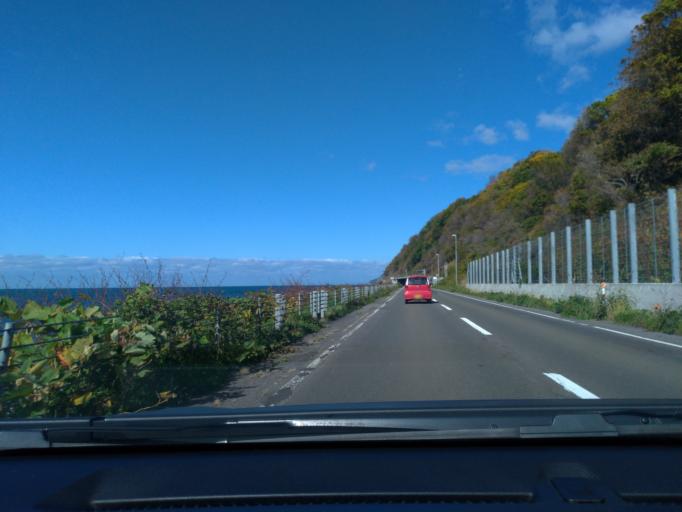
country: JP
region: Hokkaido
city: Ishikari
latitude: 43.4350
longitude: 141.4183
